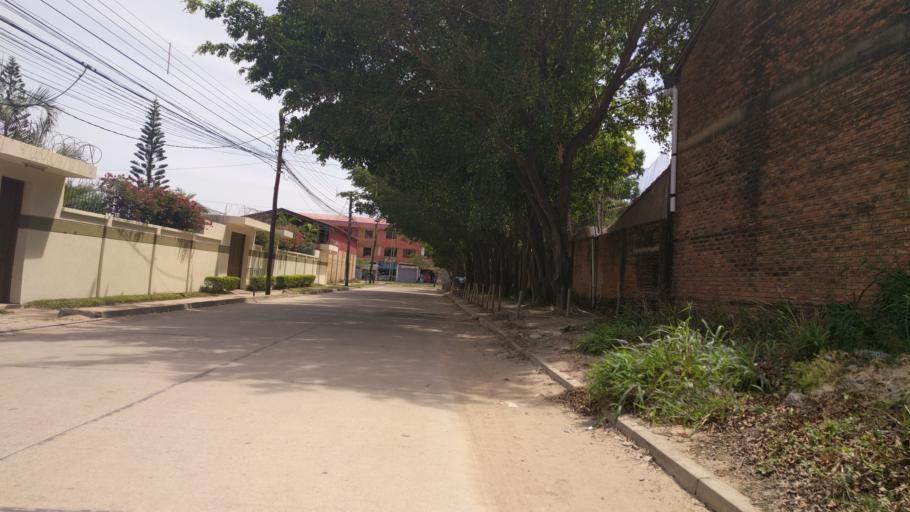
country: BO
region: Santa Cruz
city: Santa Cruz de la Sierra
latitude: -17.8079
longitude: -63.2137
